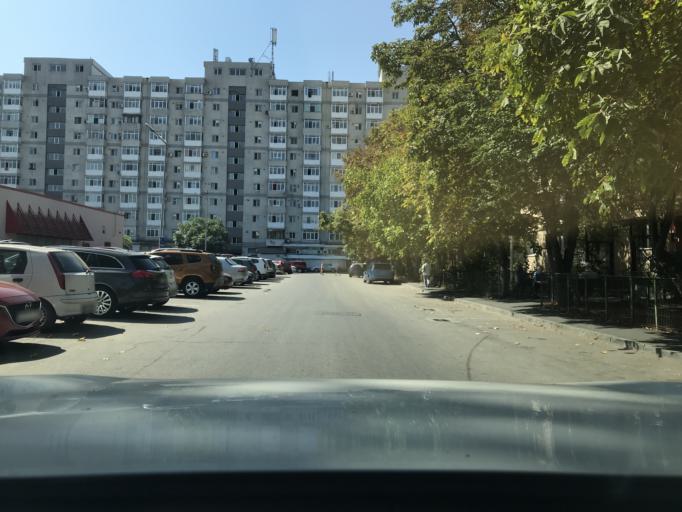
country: RO
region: Olt
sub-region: Municipiul Slatina
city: Slatina
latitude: 44.4285
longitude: 24.3704
